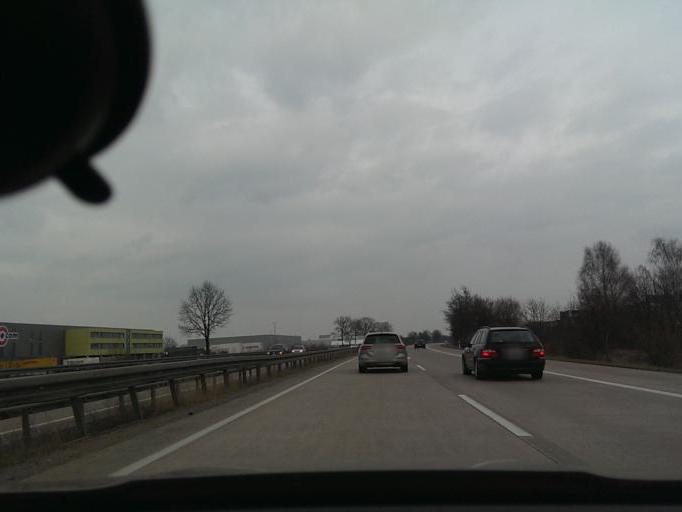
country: DE
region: Lower Saxony
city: Langenhagen
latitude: 52.4455
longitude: 9.6958
